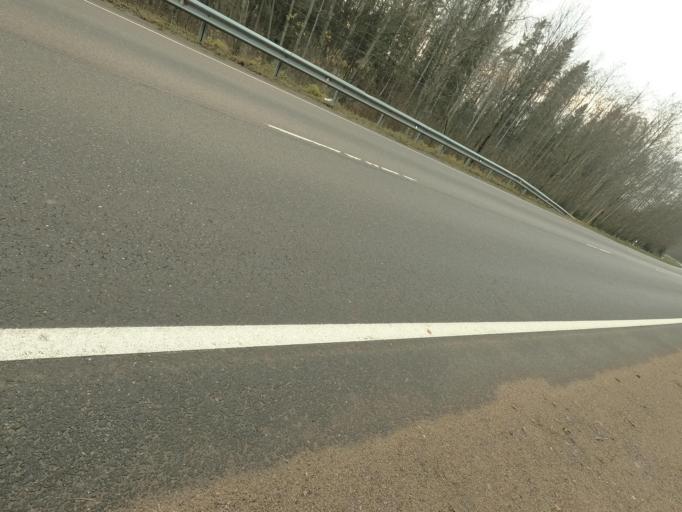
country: RU
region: Leningrad
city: Pavlovo
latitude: 59.8091
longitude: 30.9611
